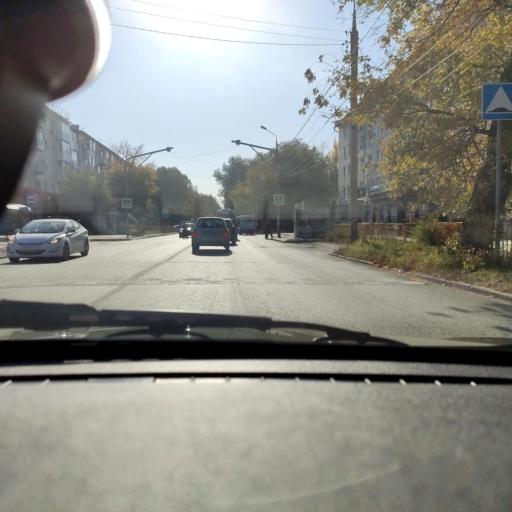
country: RU
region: Samara
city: Tol'yatti
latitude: 53.5150
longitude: 49.4237
